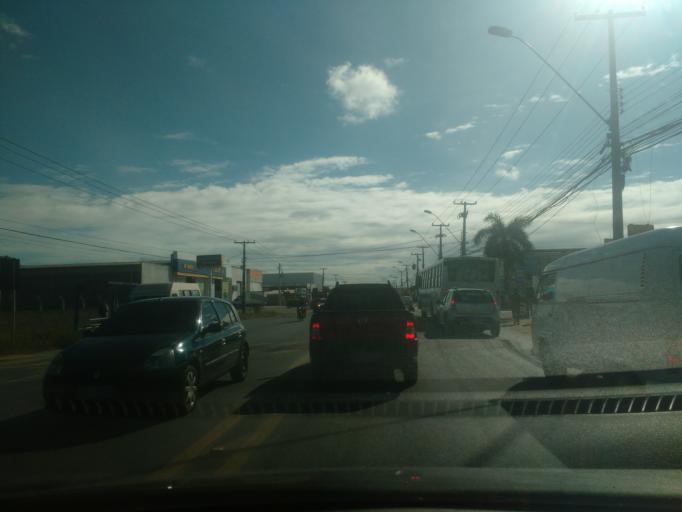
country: BR
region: Alagoas
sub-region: Satuba
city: Satuba
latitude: -9.5563
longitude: -35.7578
